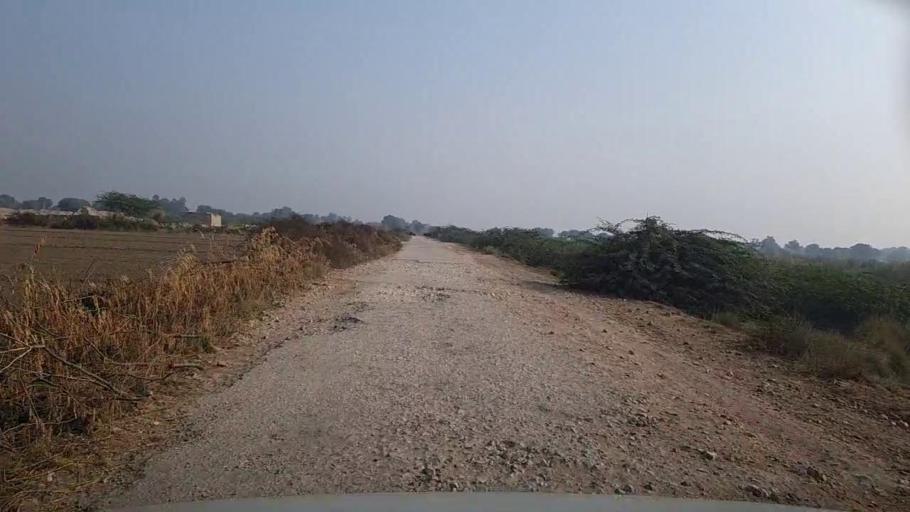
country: PK
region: Sindh
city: Setharja Old
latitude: 27.0624
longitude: 68.4563
